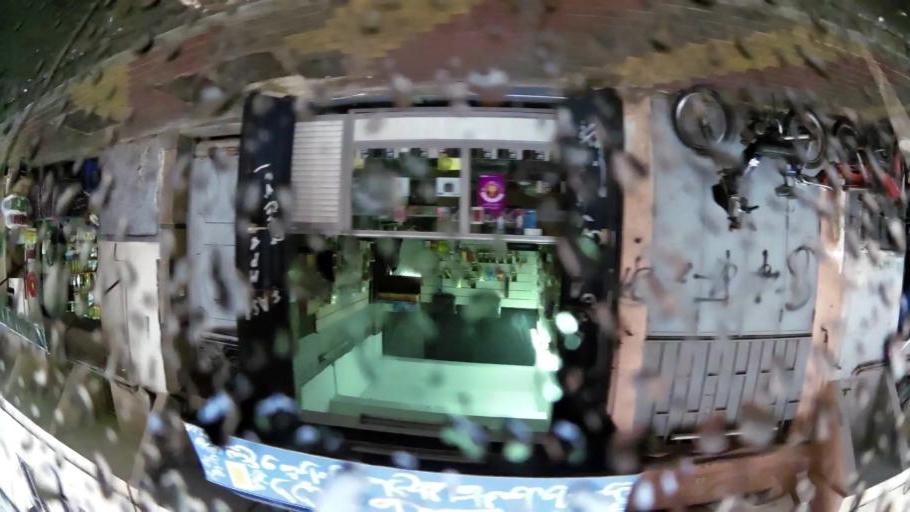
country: MA
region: Grand Casablanca
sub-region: Casablanca
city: Casablanca
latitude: 33.5647
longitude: -7.6080
